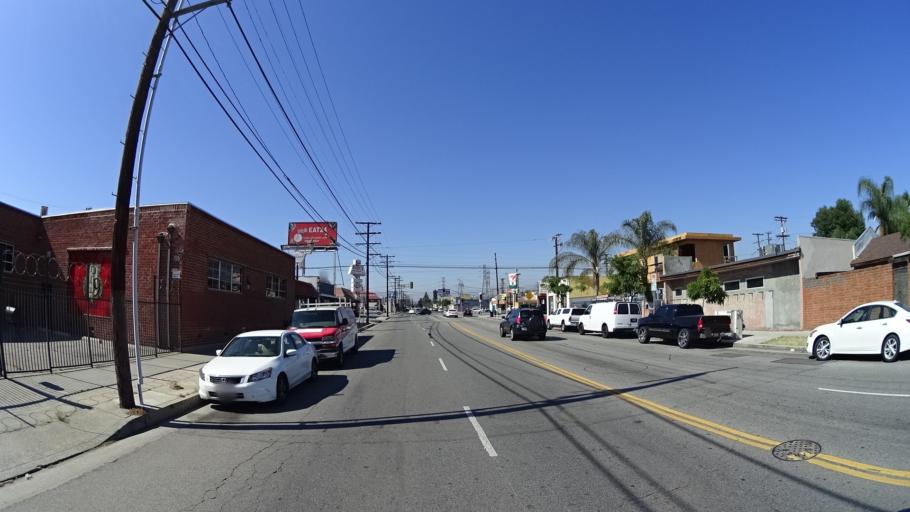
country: US
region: California
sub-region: Los Angeles County
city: North Hollywood
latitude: 34.1713
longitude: -118.3617
